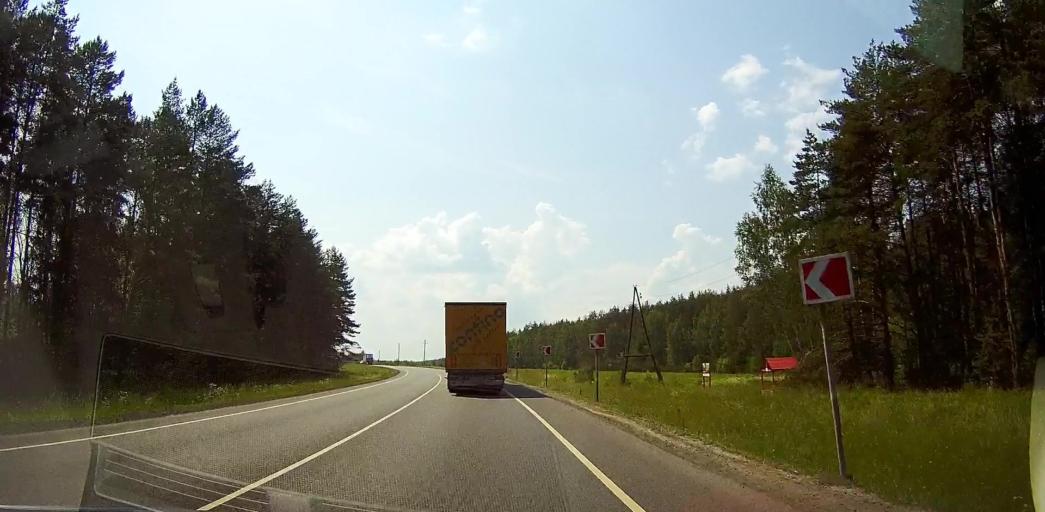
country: RU
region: Moskovskaya
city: Meshcherino
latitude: 55.1781
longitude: 38.3394
